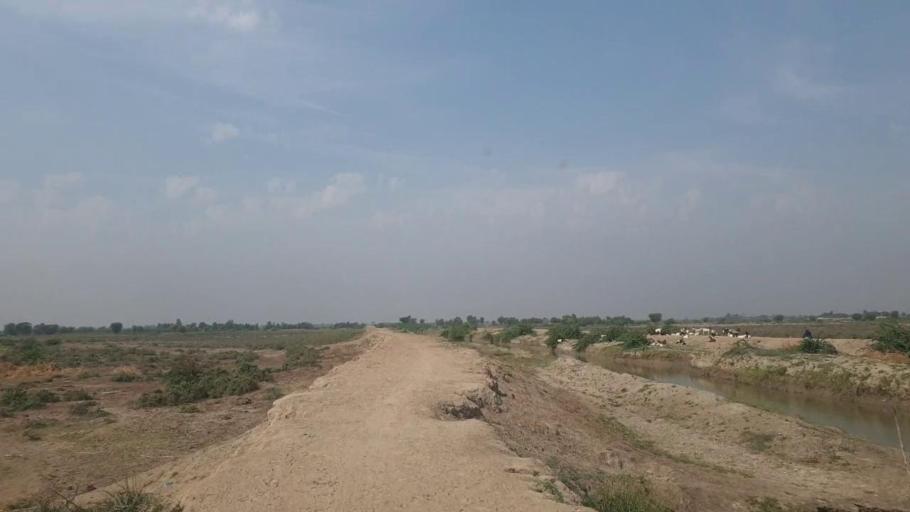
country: PK
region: Sindh
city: Rajo Khanani
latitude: 24.9579
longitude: 69.0266
